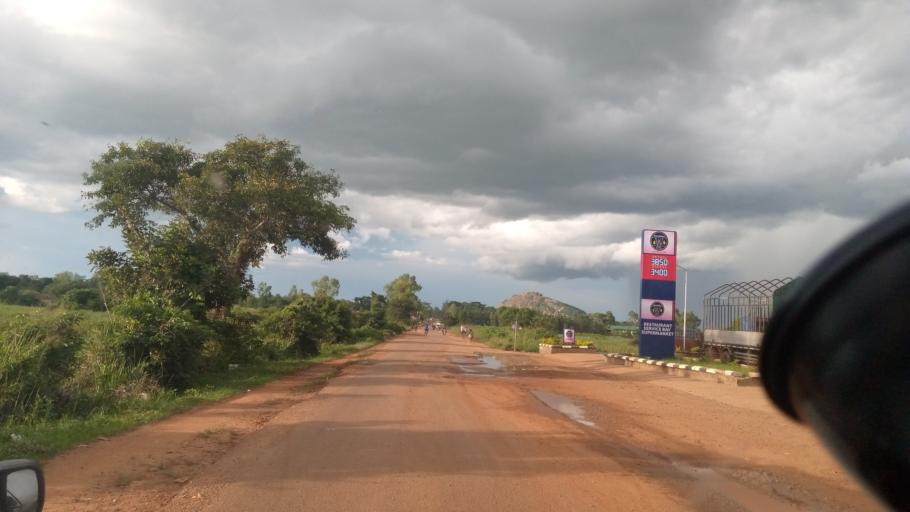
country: UG
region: Northern Region
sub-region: Lira District
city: Lira
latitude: 2.2694
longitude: 32.9144
